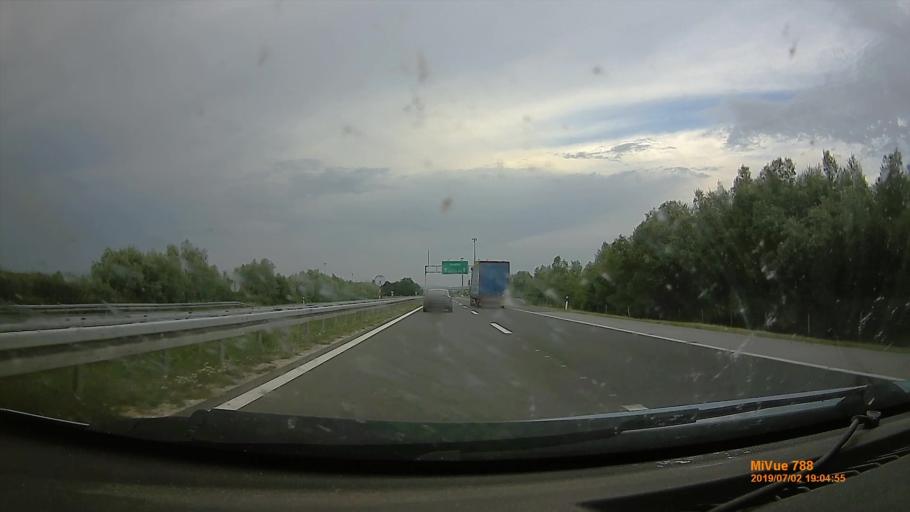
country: HR
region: Zagrebacka
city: Brckovljani
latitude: 45.9891
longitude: 16.2862
